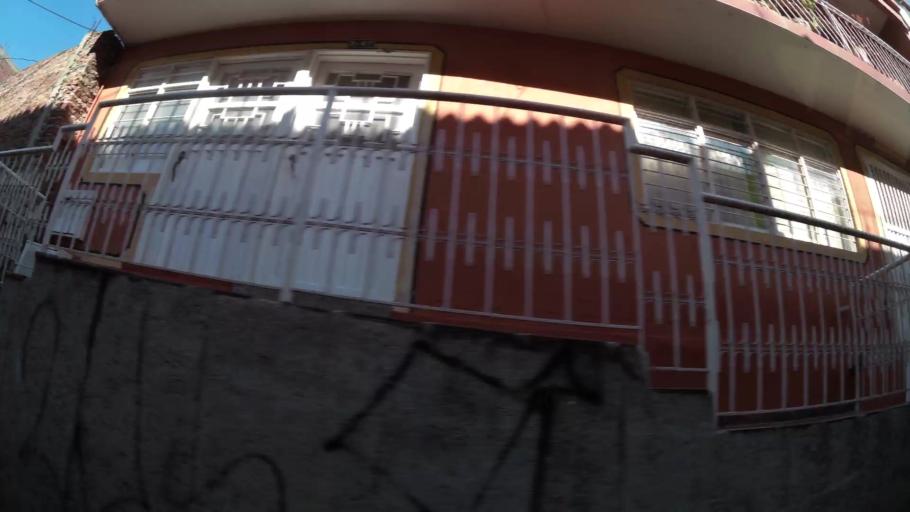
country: CO
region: Valle del Cauca
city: Cali
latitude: 3.4455
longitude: -76.5540
